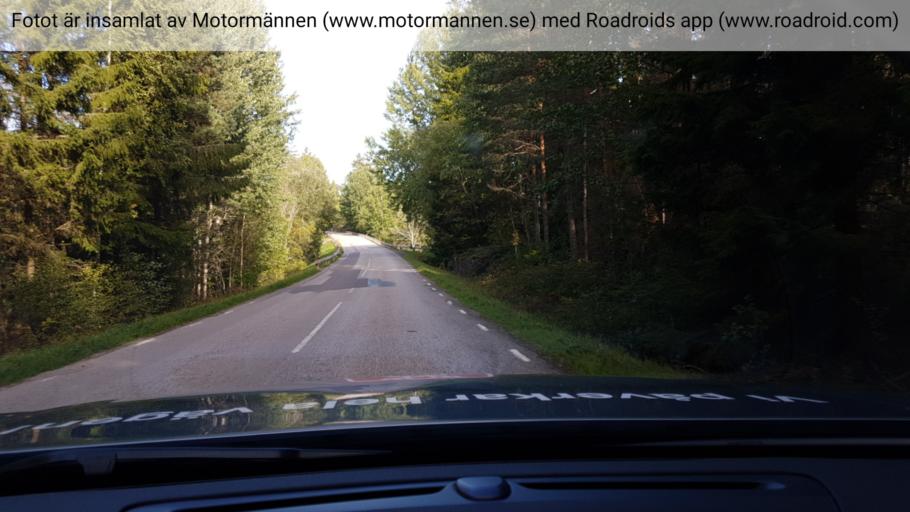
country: SE
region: Kalmar
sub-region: Vasterviks Kommun
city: Forserum
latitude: 58.0297
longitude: 16.5871
